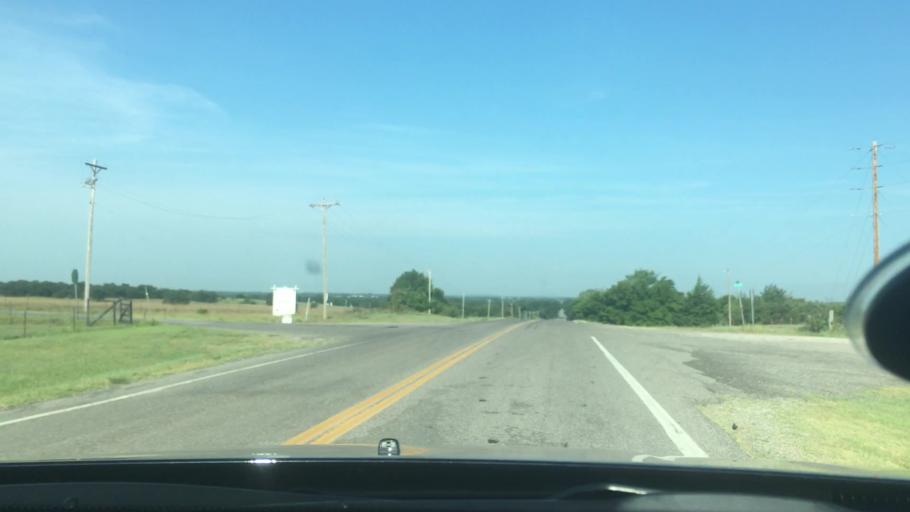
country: US
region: Oklahoma
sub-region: Garvin County
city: Pauls Valley
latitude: 34.6518
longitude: -97.2820
